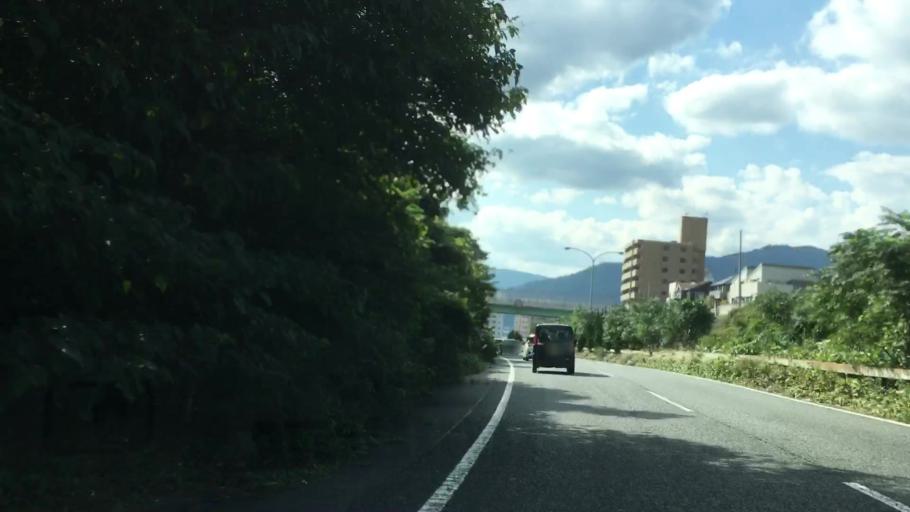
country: JP
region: Hiroshima
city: Hatsukaichi
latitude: 34.3767
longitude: 132.3731
